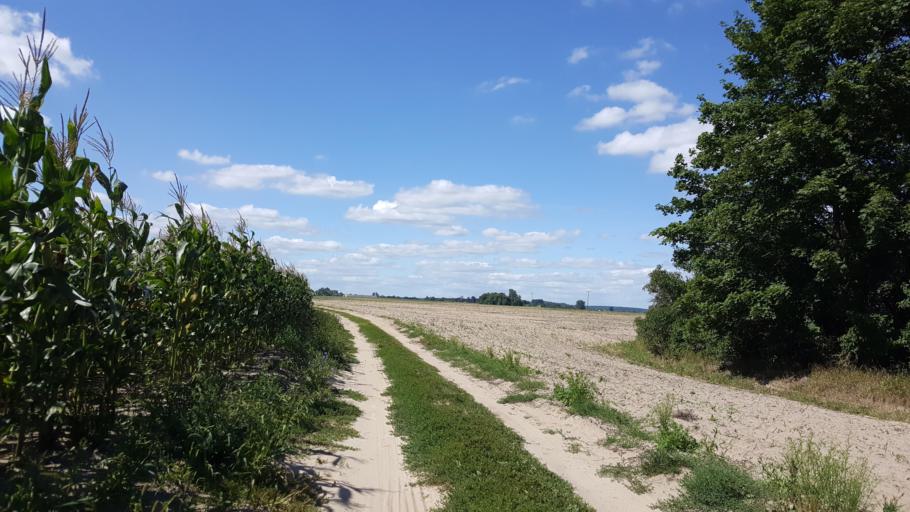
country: BY
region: Brest
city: Kobryn
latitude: 52.3047
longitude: 24.3209
